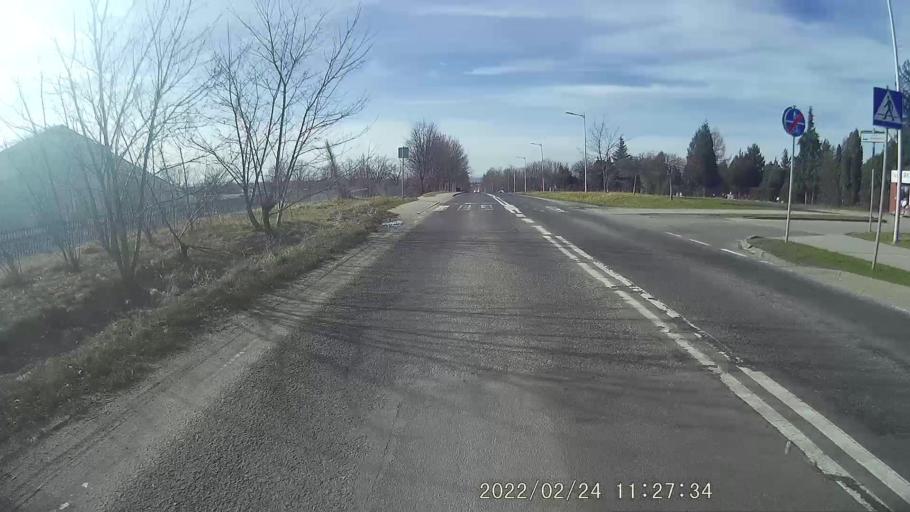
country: PL
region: Lubusz
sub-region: Powiat zaganski
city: Szprotawa
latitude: 51.5328
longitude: 15.6629
